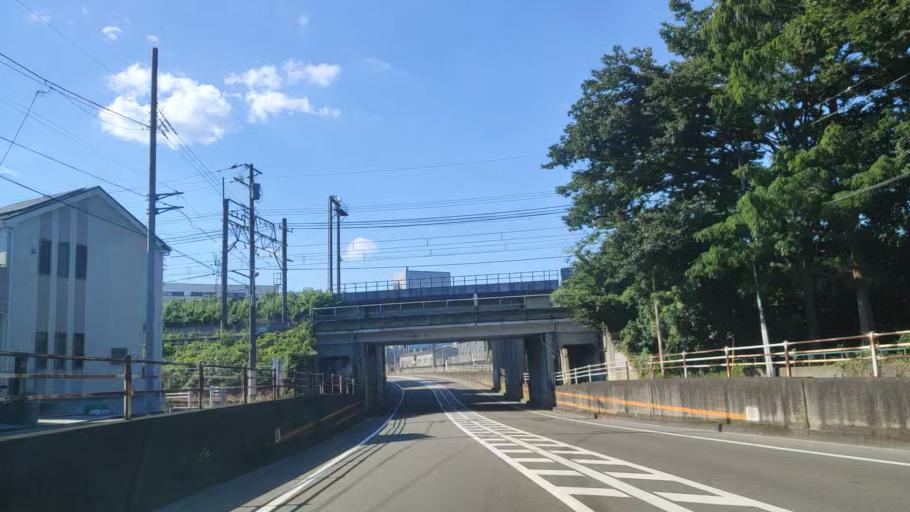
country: JP
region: Tokyo
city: Hachioji
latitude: 35.6498
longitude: 139.3580
